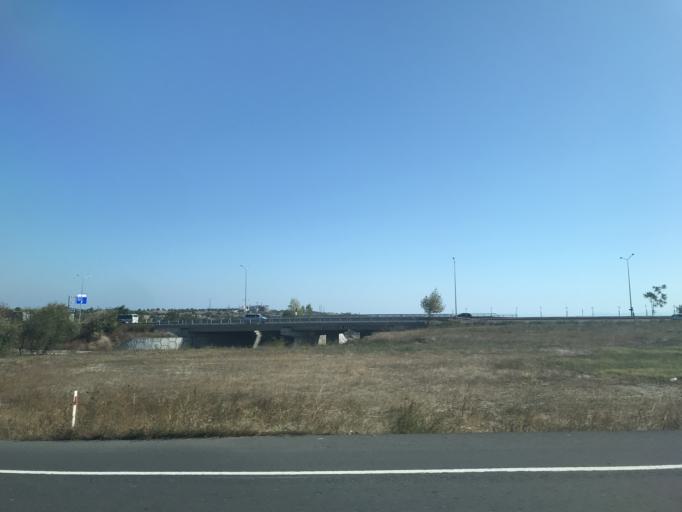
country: TR
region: Tekirdag
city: Tekirdag
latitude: 40.9967
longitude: 27.5098
